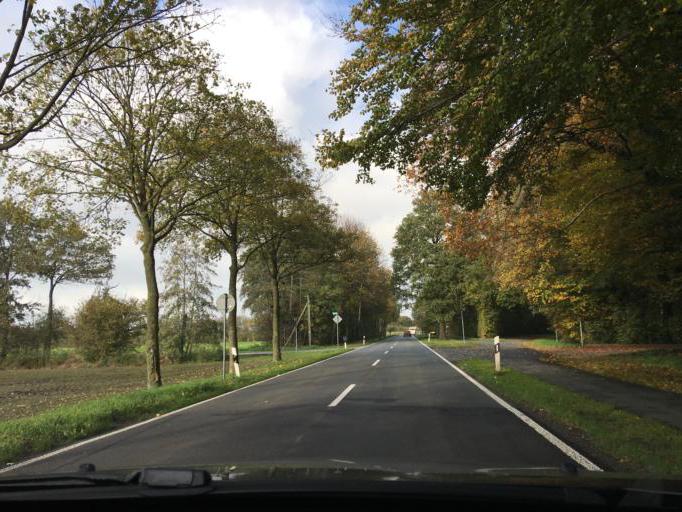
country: DE
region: North Rhine-Westphalia
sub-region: Regierungsbezirk Munster
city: Vreden
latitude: 52.0589
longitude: 6.7655
